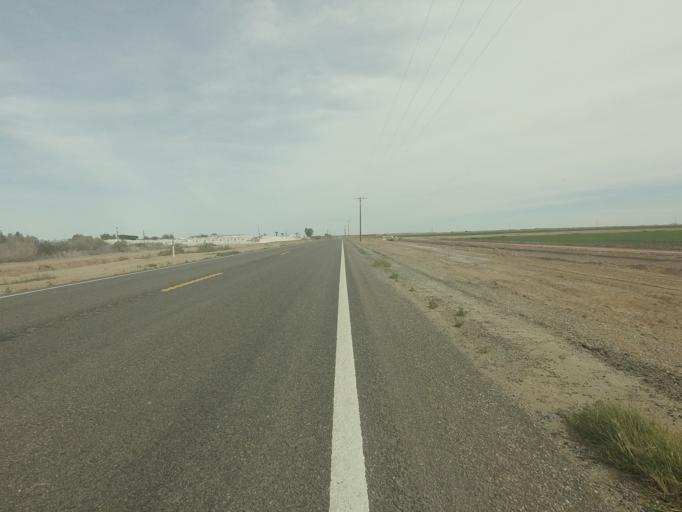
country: US
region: California
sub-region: Imperial County
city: Holtville
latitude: 32.9747
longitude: -115.3293
